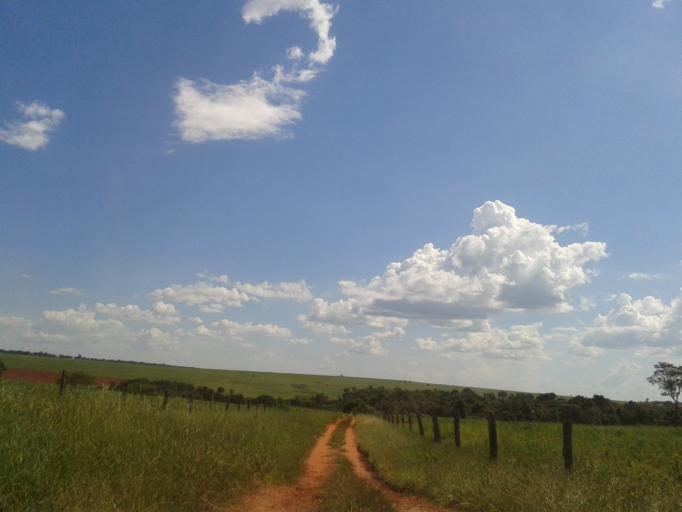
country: BR
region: Minas Gerais
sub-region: Santa Vitoria
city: Santa Vitoria
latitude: -19.1152
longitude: -50.4999
